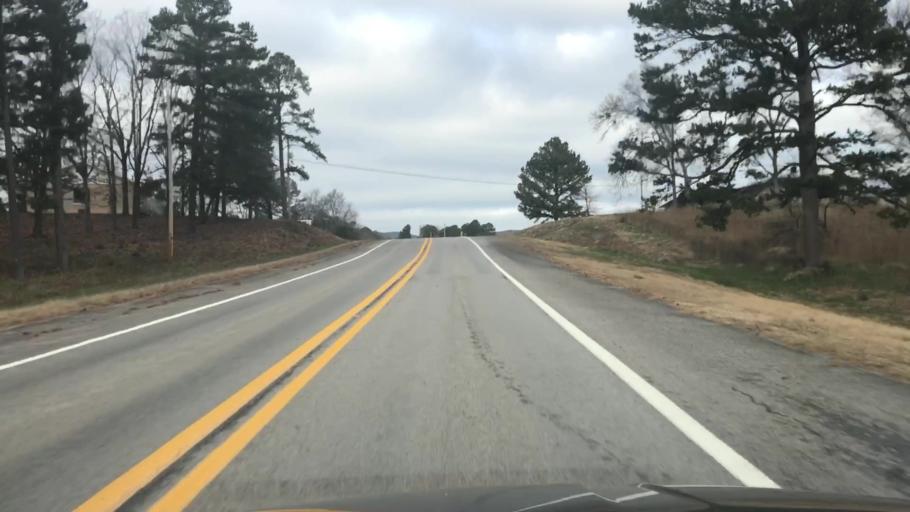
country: US
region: Arkansas
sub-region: Montgomery County
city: Mount Ida
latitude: 34.6483
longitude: -93.7503
